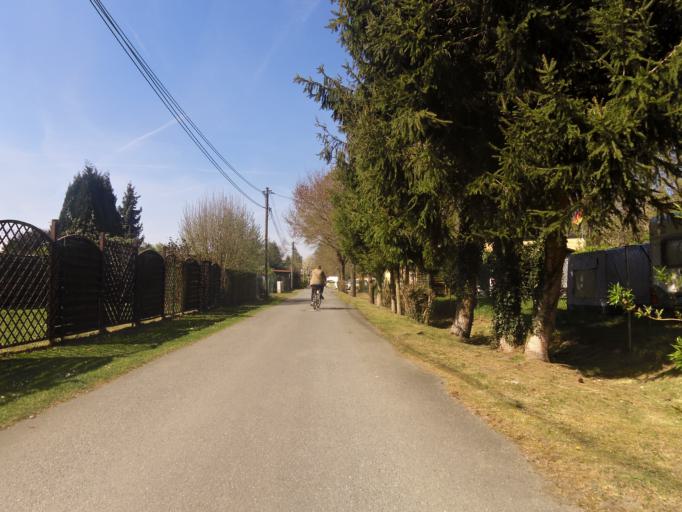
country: DE
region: Hesse
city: Morfelden-Walldorf
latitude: 49.9785
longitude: 8.5953
